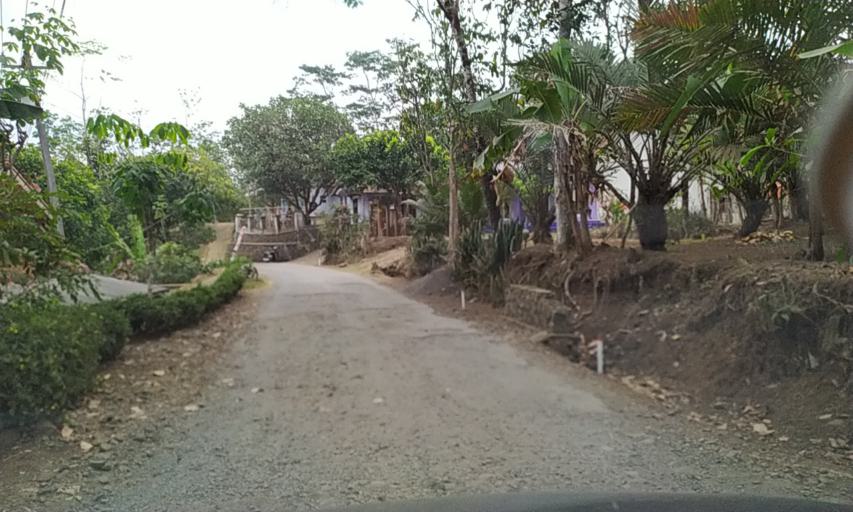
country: ID
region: Central Java
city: Ciwalen
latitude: -7.2877
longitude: 108.6115
